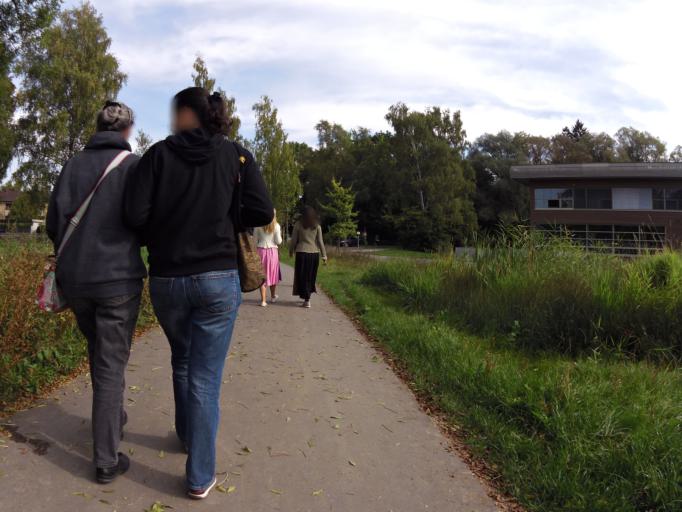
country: DE
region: Bavaria
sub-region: Upper Bavaria
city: Starnberg
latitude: 47.9982
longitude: 11.3484
